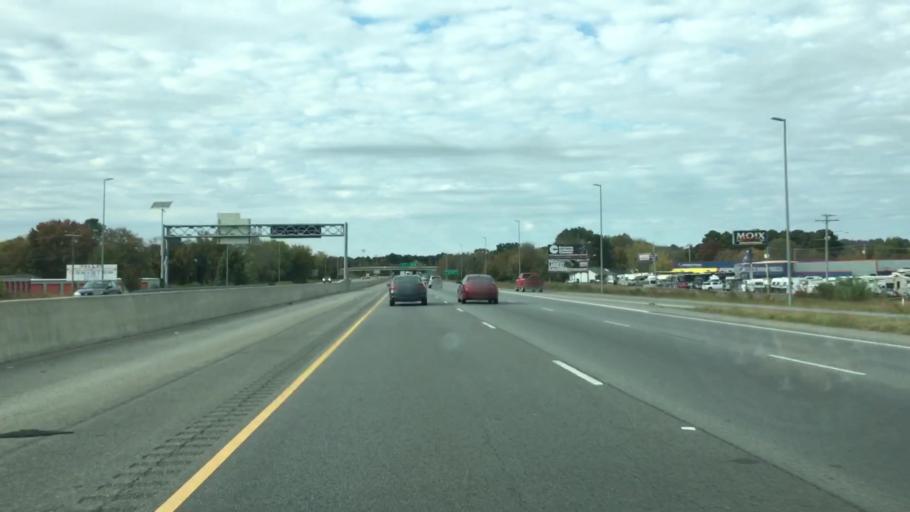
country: US
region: Arkansas
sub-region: Faulkner County
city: Conway
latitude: 35.0947
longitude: -92.4257
